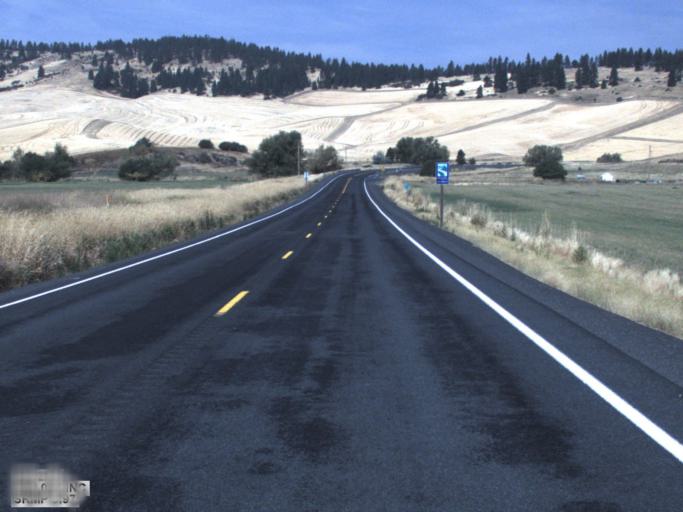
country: US
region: Washington
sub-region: Whitman County
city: Pullman
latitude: 46.8558
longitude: -117.1277
